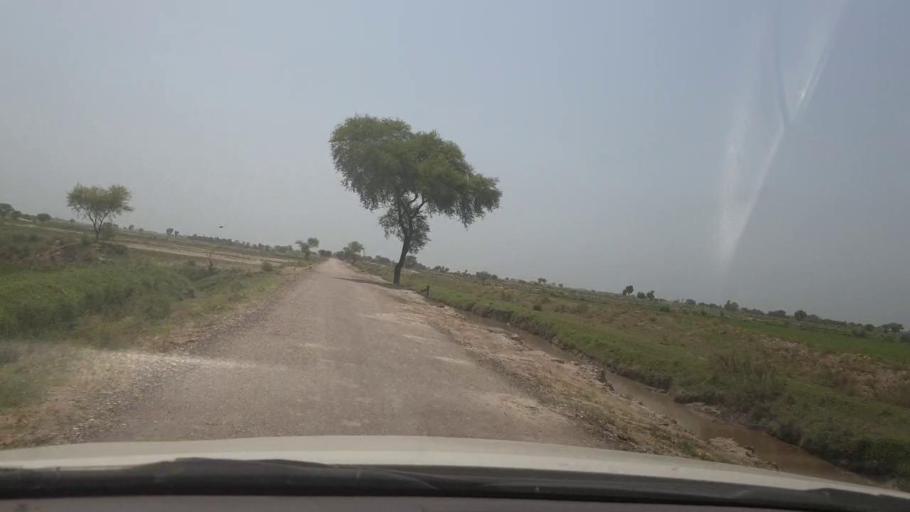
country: PK
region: Sindh
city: Shikarpur
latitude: 28.0446
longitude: 68.5699
